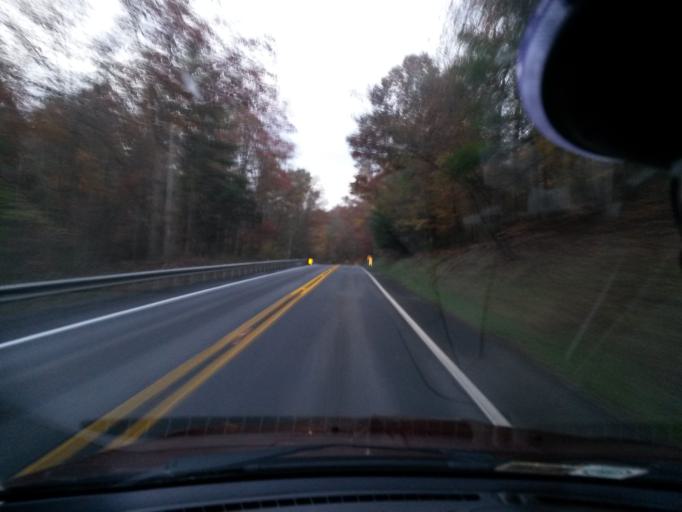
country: US
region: Virginia
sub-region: Alleghany County
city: Clifton Forge
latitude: 37.7040
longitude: -79.8155
